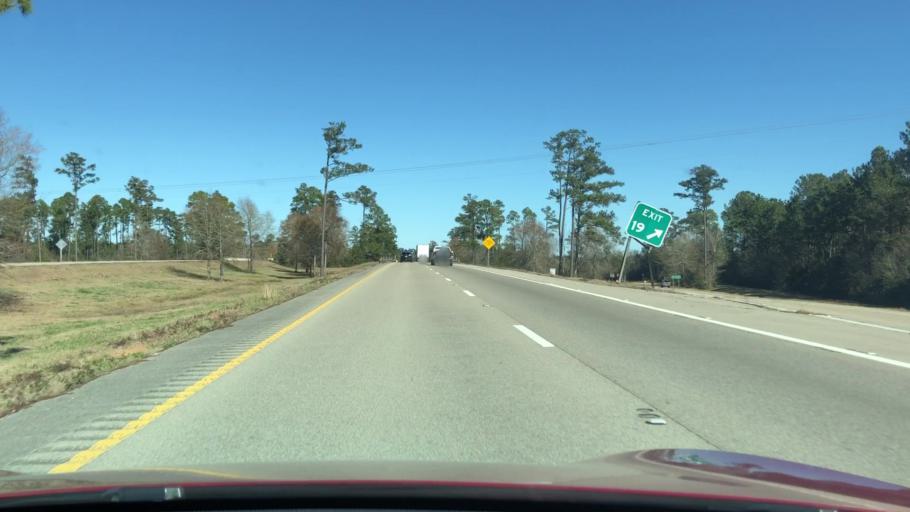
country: US
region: Mississippi
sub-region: Pearl River County
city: Poplarville
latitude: 30.7158
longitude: -89.5554
